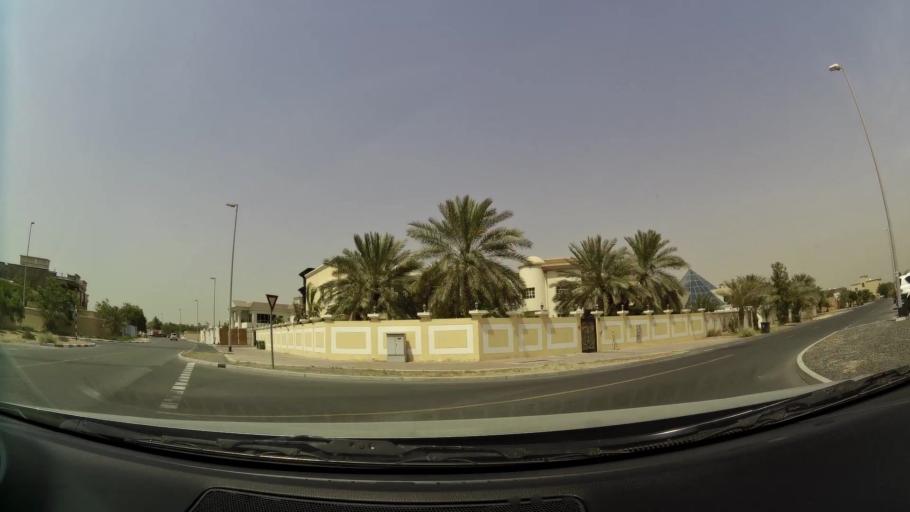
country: AE
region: Ash Shariqah
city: Sharjah
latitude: 25.2433
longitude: 55.4257
